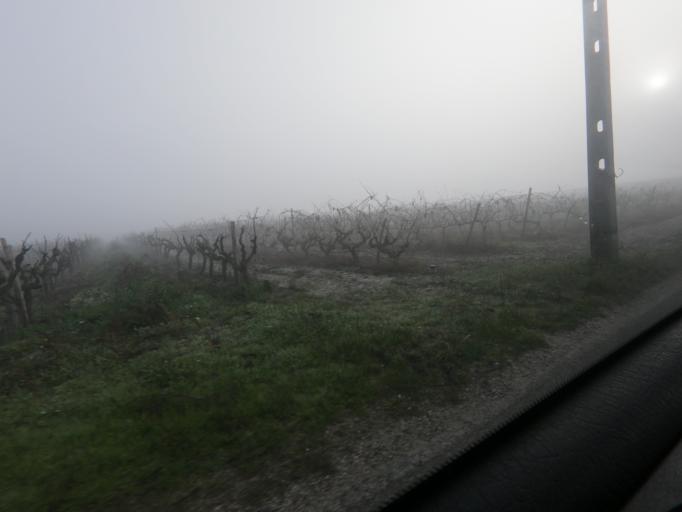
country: PT
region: Setubal
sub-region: Palmela
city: Palmela
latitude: 38.5973
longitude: -8.8441
